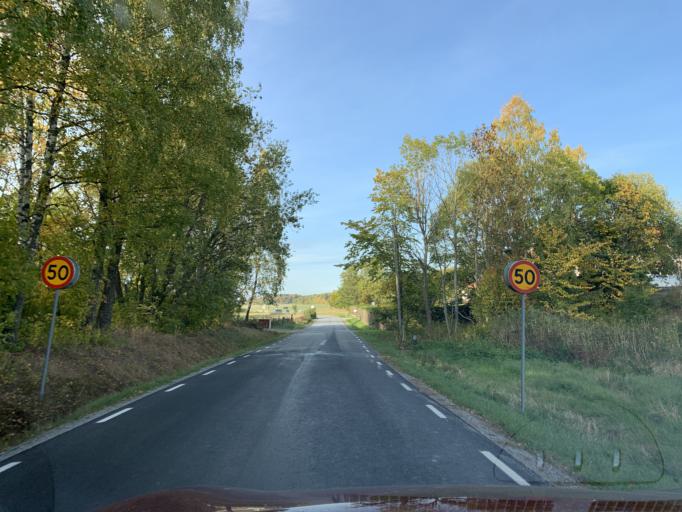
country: SE
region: Stockholm
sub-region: Upplands-Bro Kommun
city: Bro
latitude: 59.5043
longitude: 17.5858
